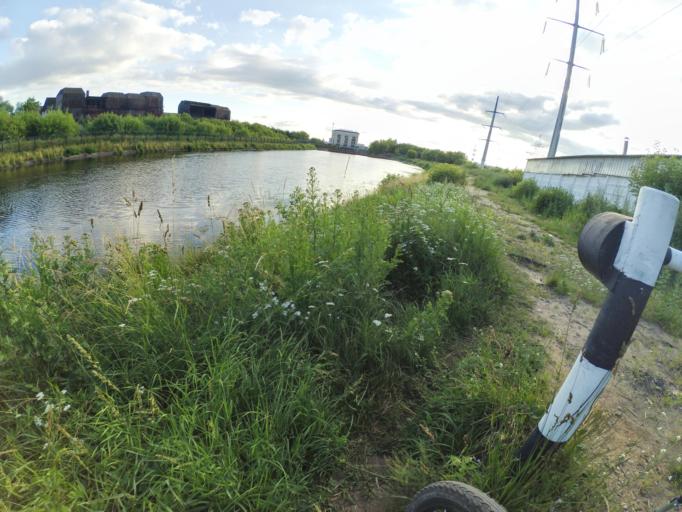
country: RU
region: Moscow
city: Strogino
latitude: 55.8368
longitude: 37.4377
